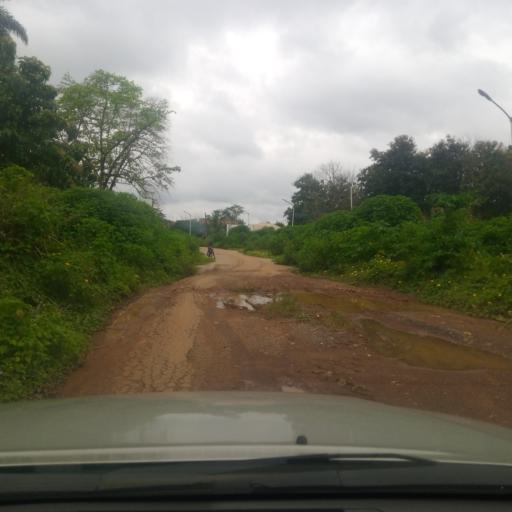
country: NG
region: Ebonyi
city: Effium
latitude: 6.6276
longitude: 8.0531
